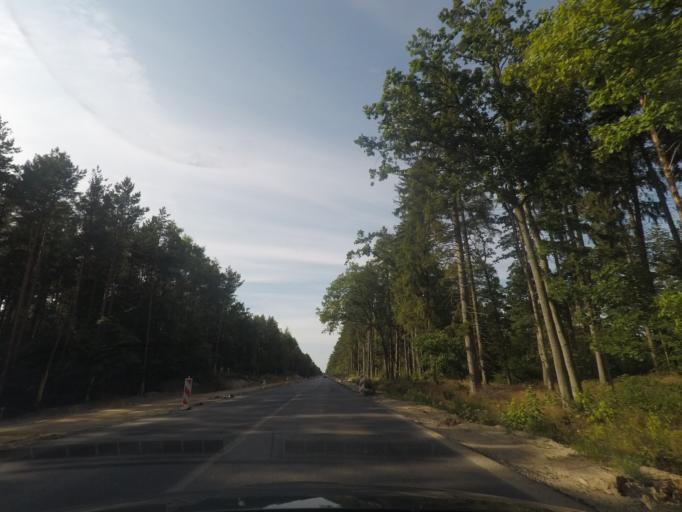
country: PL
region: Pomeranian Voivodeship
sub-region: Powiat leborski
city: Leba
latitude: 54.6968
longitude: 17.5901
